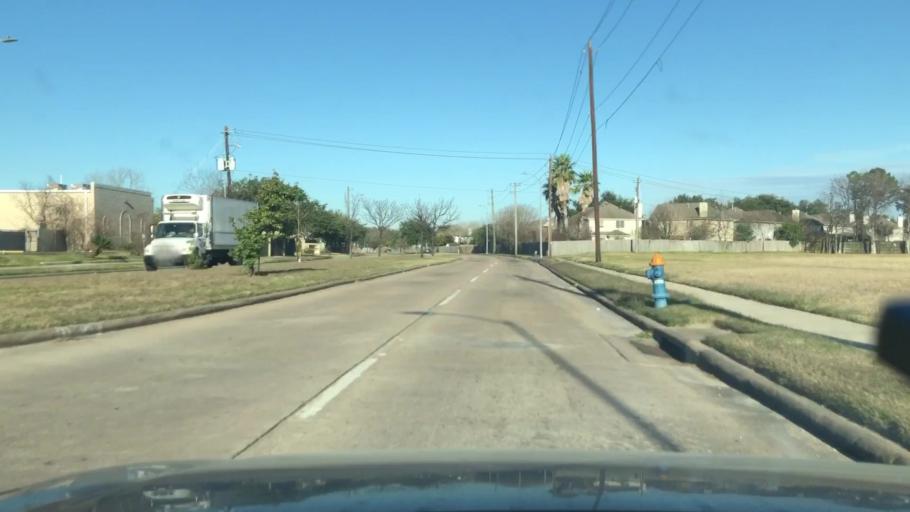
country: US
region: Texas
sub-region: Fort Bend County
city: Missouri City
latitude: 29.6433
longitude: -95.5301
